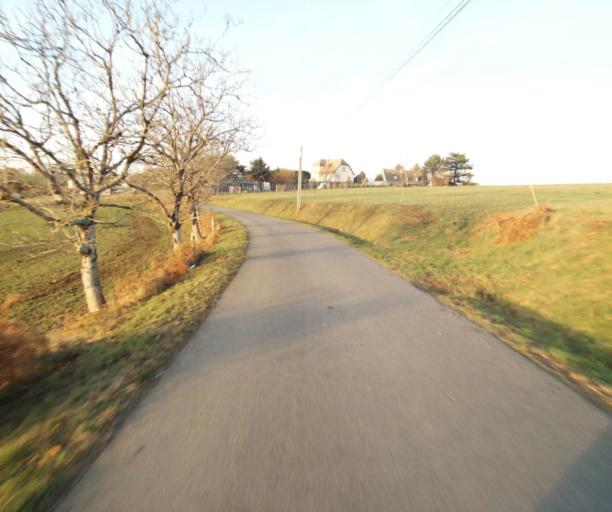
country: FR
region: Limousin
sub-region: Departement de la Correze
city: Laguenne
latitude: 45.2269
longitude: 1.8264
